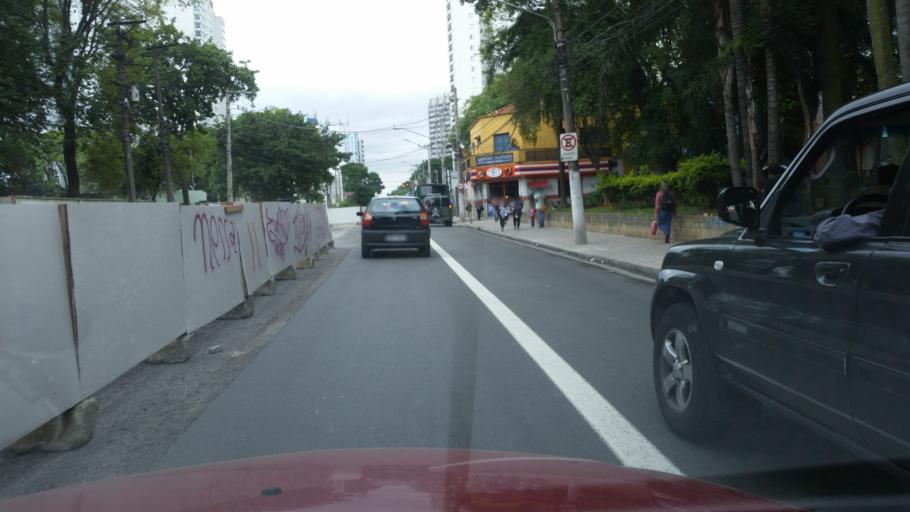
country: BR
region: Sao Paulo
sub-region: Diadema
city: Diadema
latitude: -23.6483
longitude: -46.7029
